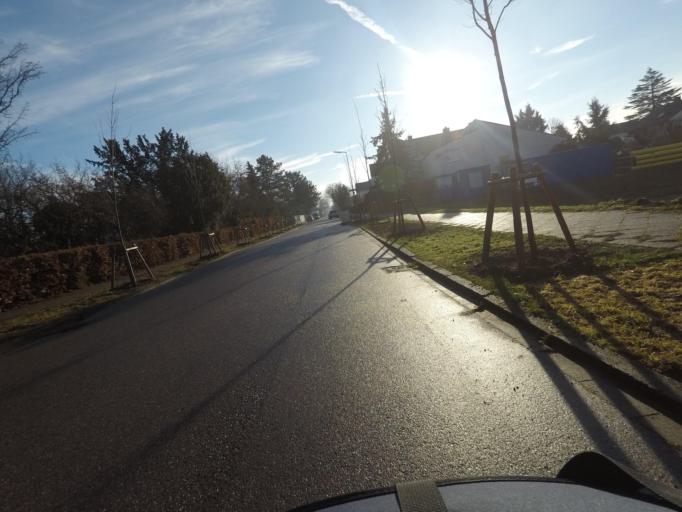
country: DE
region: Baden-Wuerttemberg
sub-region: Karlsruhe Region
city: Ettlingen
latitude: 48.9714
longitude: 8.4147
